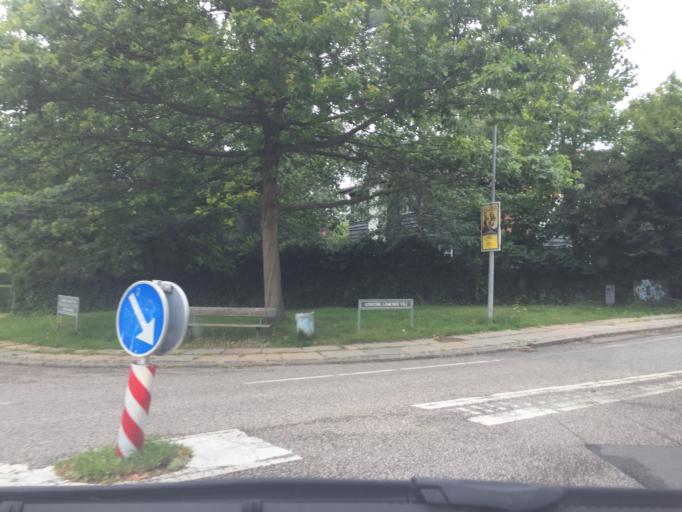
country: DK
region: Capital Region
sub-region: Lyngby-Tarbaek Kommune
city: Kongens Lyngby
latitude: 55.7865
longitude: 12.5027
